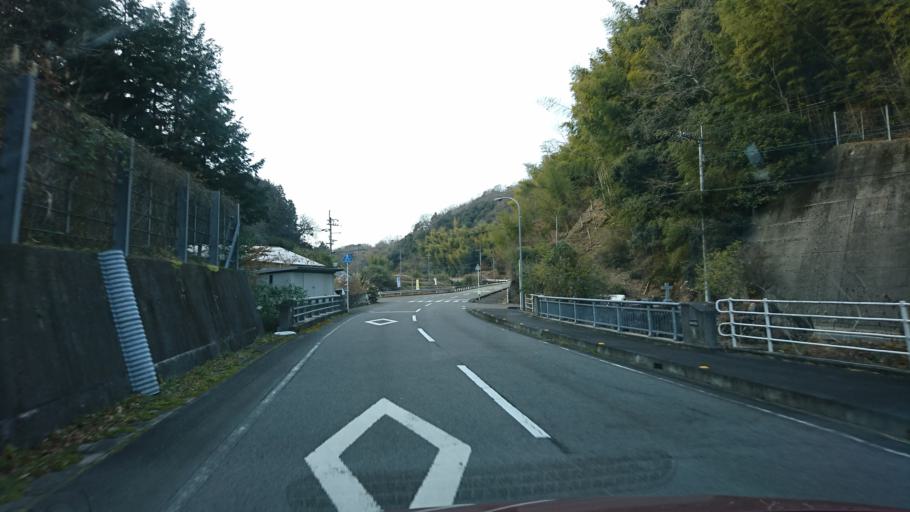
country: JP
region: Ehime
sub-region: Shikoku-chuo Shi
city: Matsuyama
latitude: 33.8996
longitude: 132.8255
